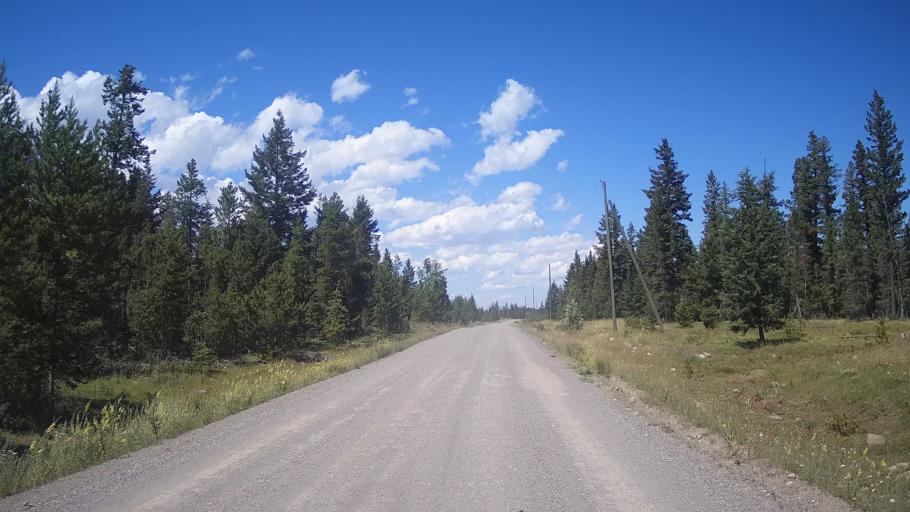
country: CA
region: British Columbia
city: Cache Creek
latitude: 51.2185
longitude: -121.6120
